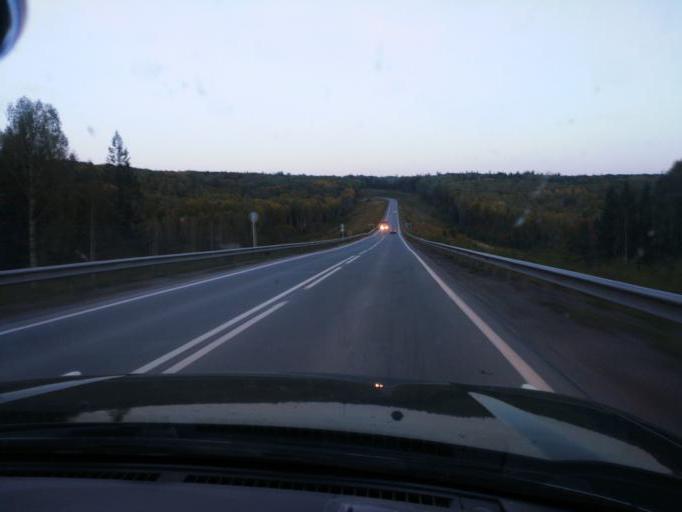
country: RU
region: Perm
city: Sylva
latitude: 58.3008
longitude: 56.7916
